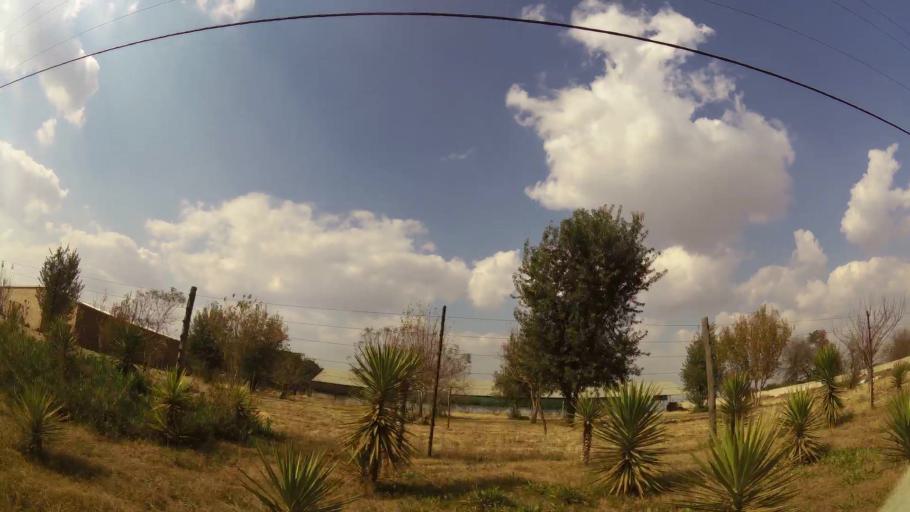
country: ZA
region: Mpumalanga
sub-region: Nkangala District Municipality
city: Delmas
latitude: -26.1508
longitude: 28.5450
